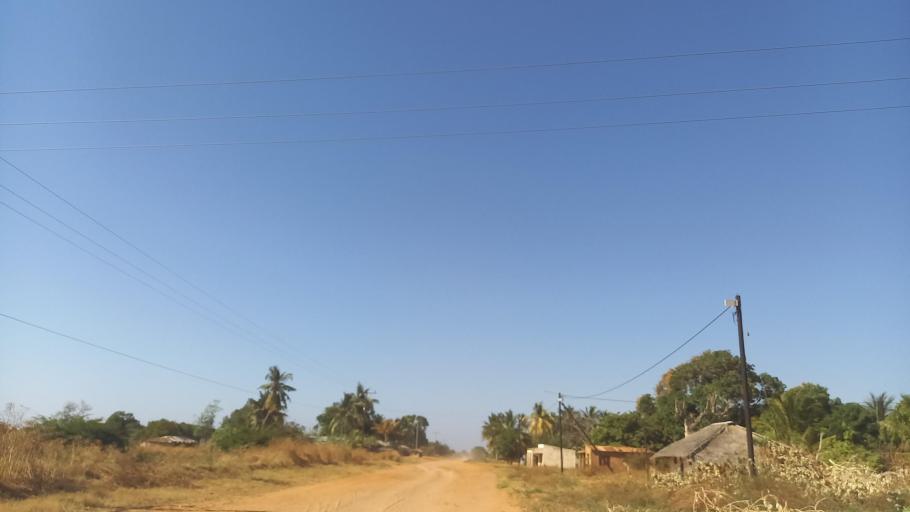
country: MZ
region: Cabo Delgado
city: Pemba
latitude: -13.1452
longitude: 40.5563
